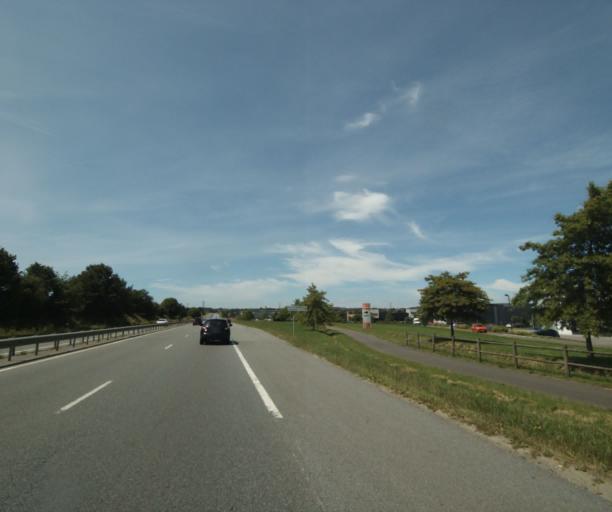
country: FR
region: Pays de la Loire
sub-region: Departement de la Mayenne
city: Change
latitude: 48.0818
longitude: -0.7984
